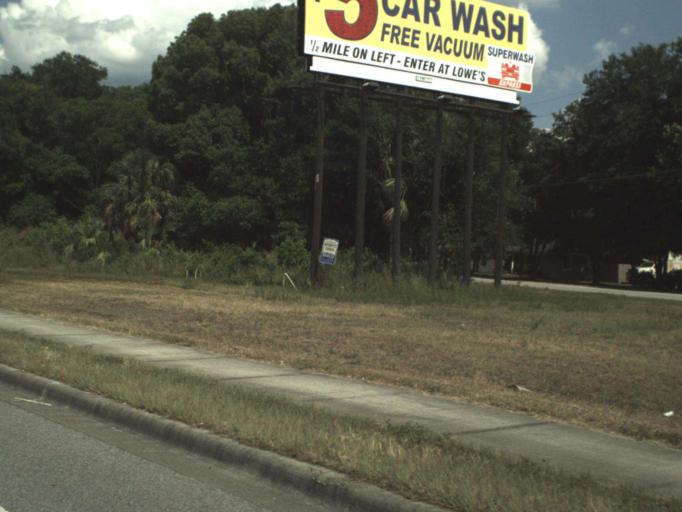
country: US
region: Florida
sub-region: Lake County
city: Mount Dora
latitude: 28.8226
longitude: -81.6625
